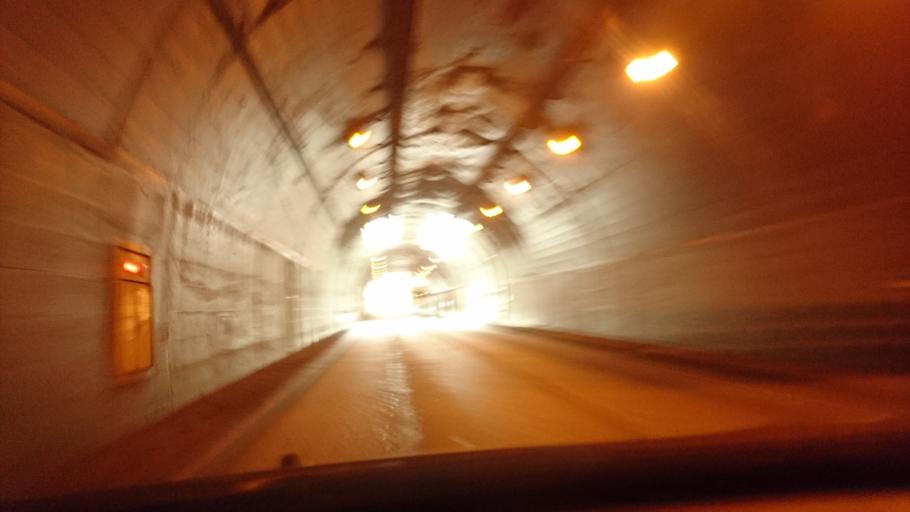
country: JP
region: Iwate
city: Miyako
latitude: 39.6905
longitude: 141.9507
